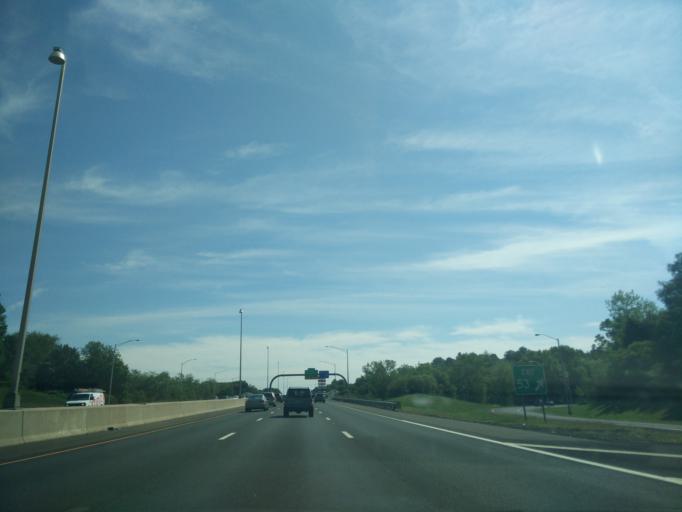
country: US
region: Connecticut
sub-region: New Haven County
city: Branford
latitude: 41.2851
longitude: -72.8399
